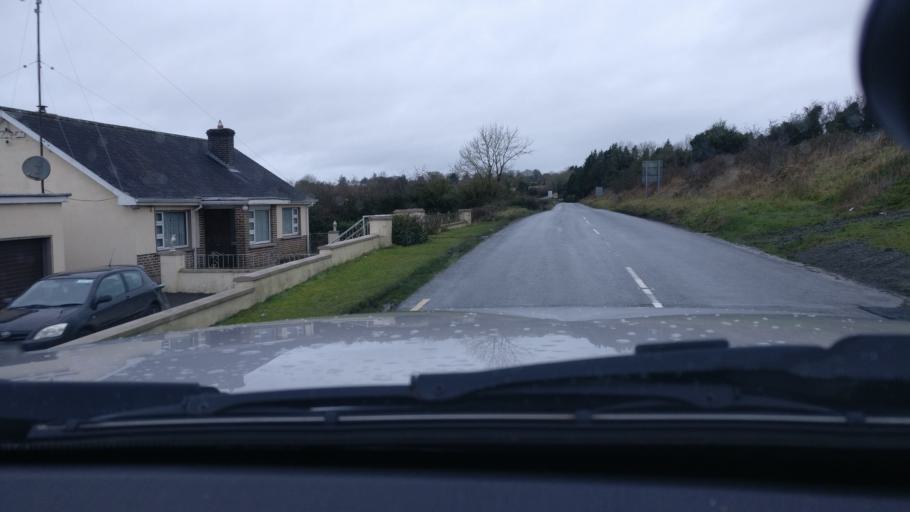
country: IE
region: Leinster
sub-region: An Longfort
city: Granard
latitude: 53.7925
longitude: -7.3985
